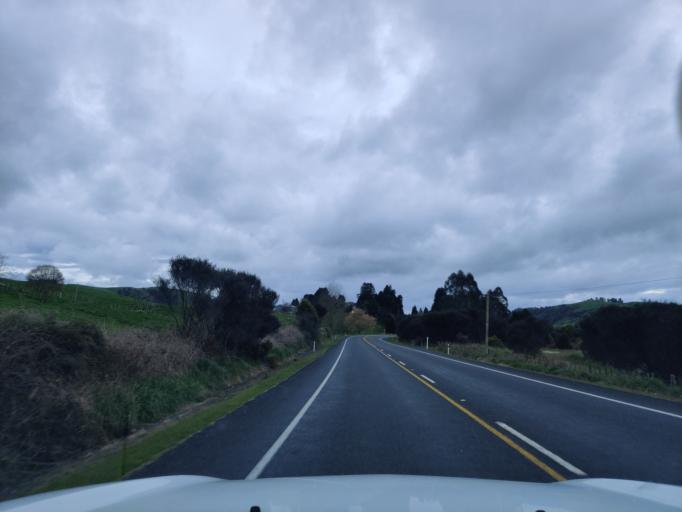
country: NZ
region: Waikato
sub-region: Otorohanga District
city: Otorohanga
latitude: -38.5024
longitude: 175.2037
